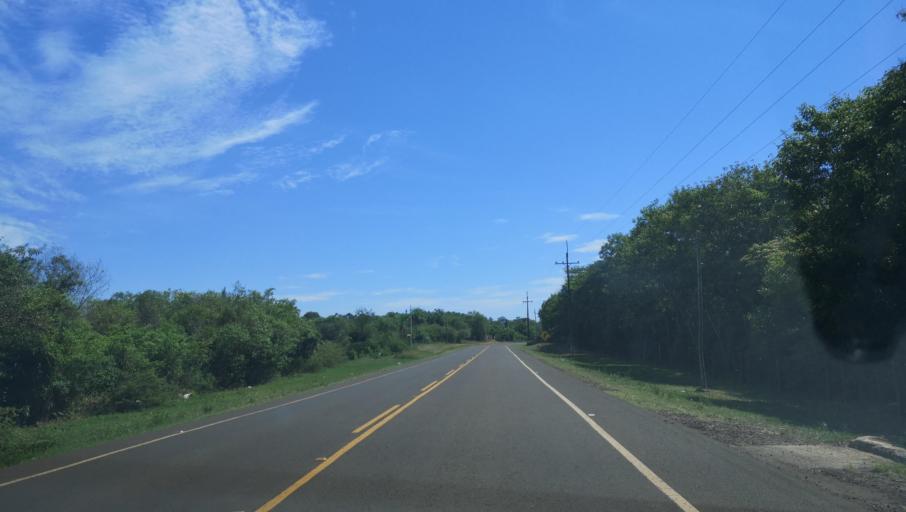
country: PY
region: Misiones
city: Santa Maria
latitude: -26.9062
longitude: -57.0282
